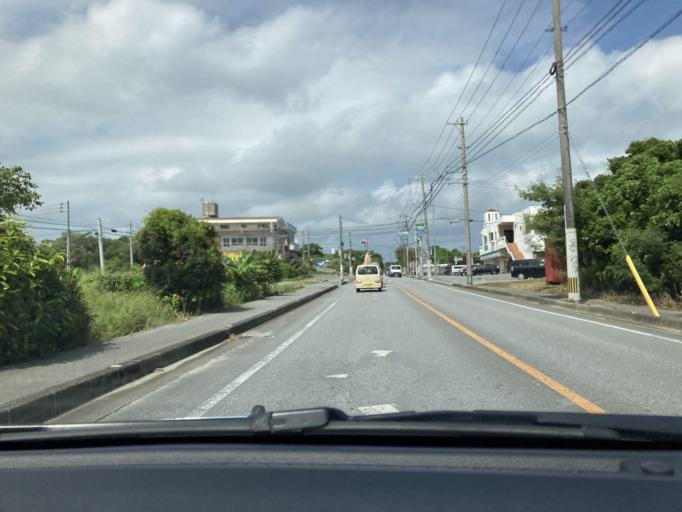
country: JP
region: Okinawa
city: Ishikawa
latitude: 26.3982
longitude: 127.8483
